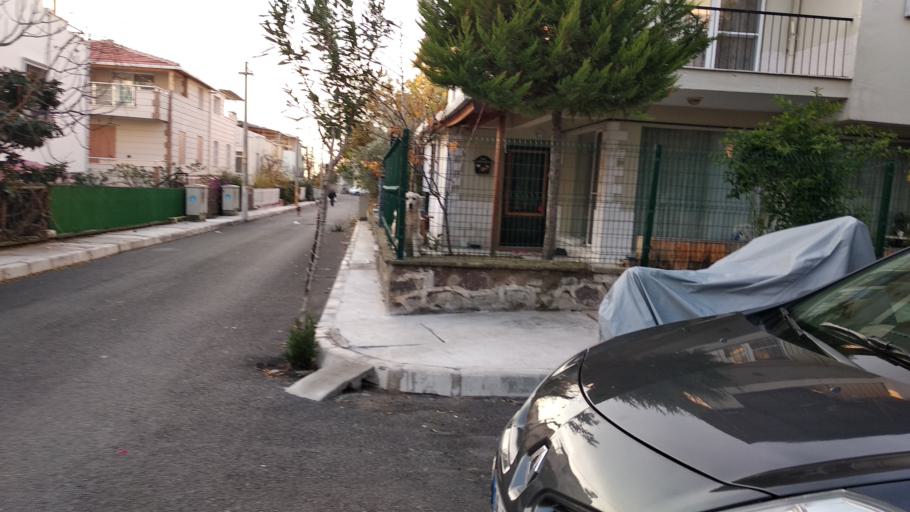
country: TR
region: Izmir
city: Karsiyaka
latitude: 38.4969
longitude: 27.0850
